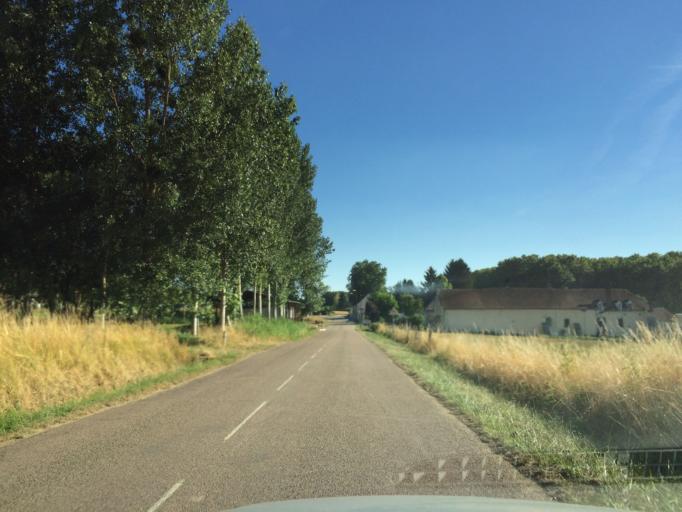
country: FR
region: Bourgogne
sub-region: Departement de l'Yonne
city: Fleury-la-Vallee
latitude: 47.8757
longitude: 3.4487
